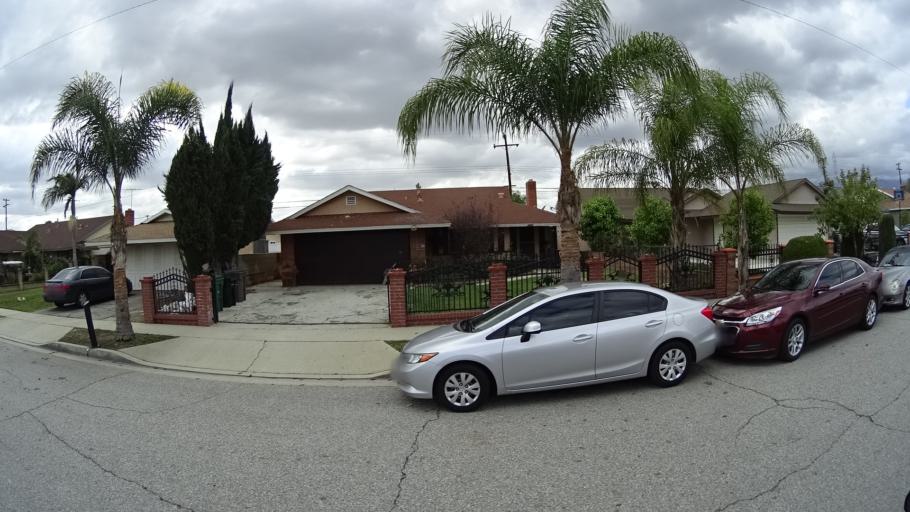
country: US
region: California
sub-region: Los Angeles County
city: Baldwin Park
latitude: 34.1009
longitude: -117.9712
